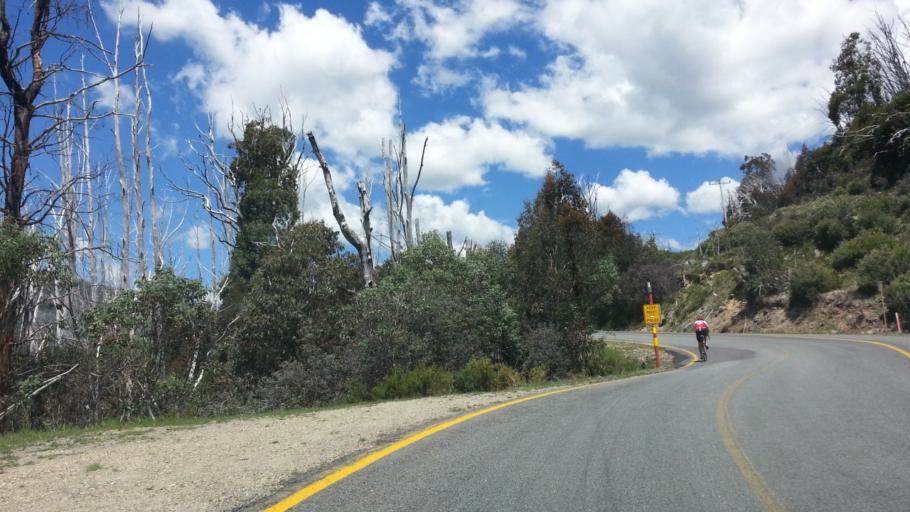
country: AU
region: Victoria
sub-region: Alpine
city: Mount Beauty
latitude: -36.8505
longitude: 147.2701
